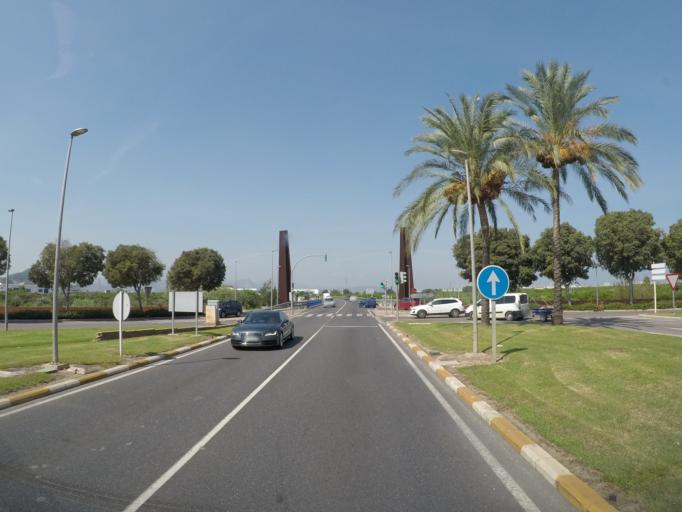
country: ES
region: Valencia
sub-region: Provincia de Valencia
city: Oliva
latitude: 38.9243
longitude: -0.1259
